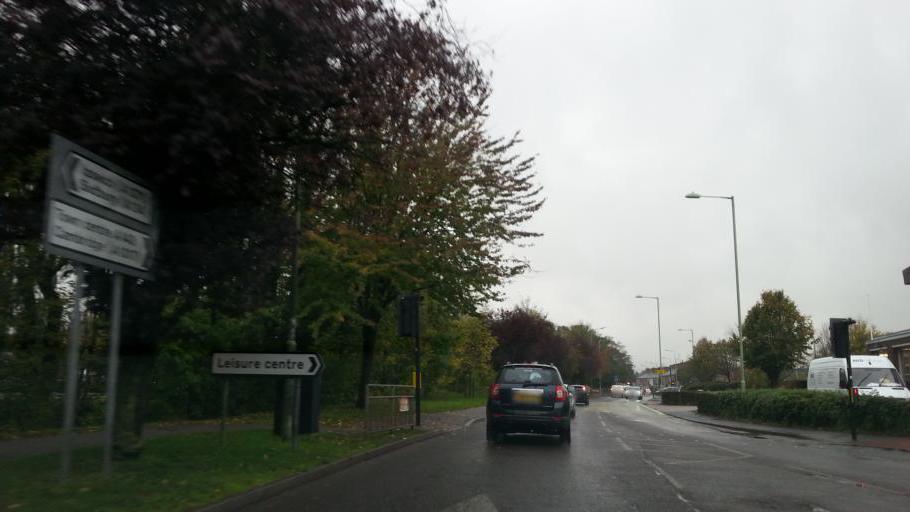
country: GB
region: England
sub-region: Suffolk
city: Haverhill
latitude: 52.0821
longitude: 0.4420
